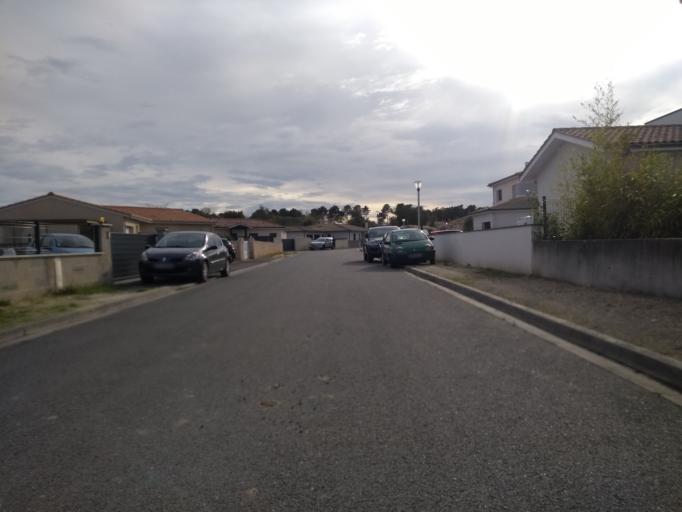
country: FR
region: Aquitaine
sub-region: Departement de la Gironde
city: Cestas
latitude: 44.7394
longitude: -0.6717
